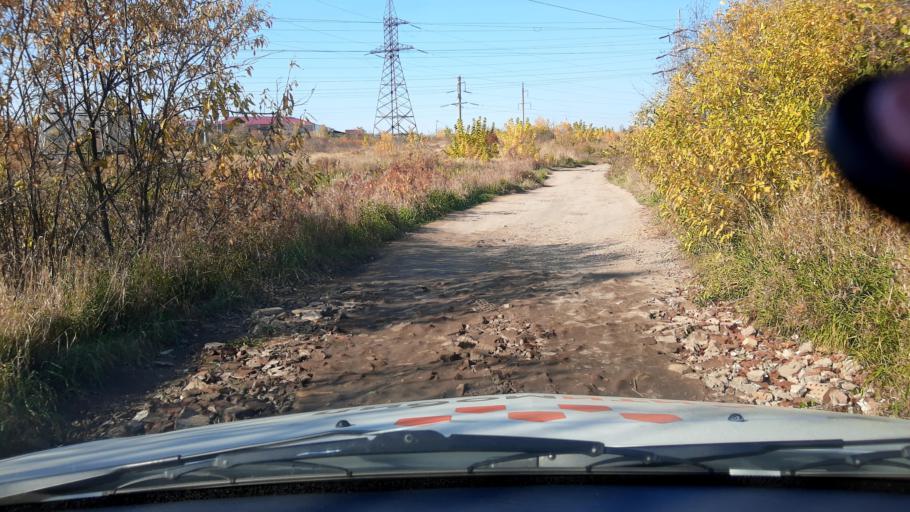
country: RU
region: Bashkortostan
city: Ufa
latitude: 54.8634
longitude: 56.1315
